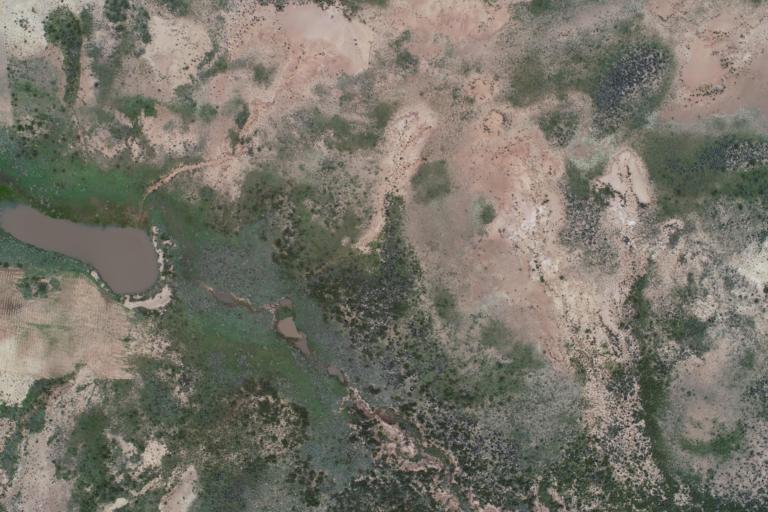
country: BO
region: La Paz
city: Curahuara de Carangas
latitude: -17.2958
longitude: -68.5090
